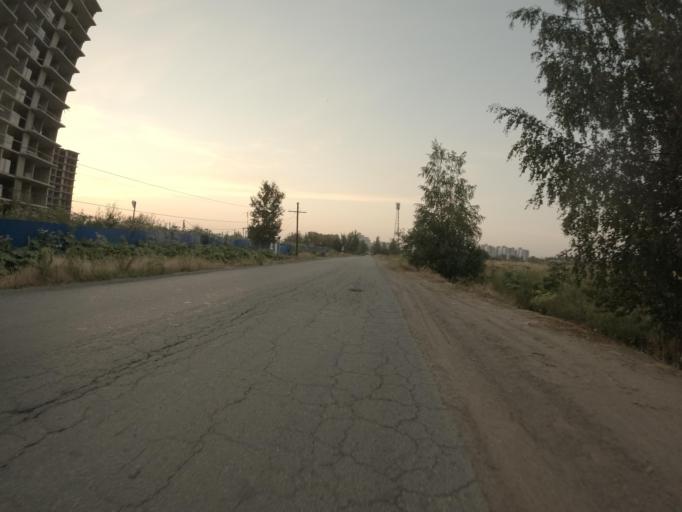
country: RU
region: Leningrad
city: Yanino Vtoroye
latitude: 59.9429
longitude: 30.5537
